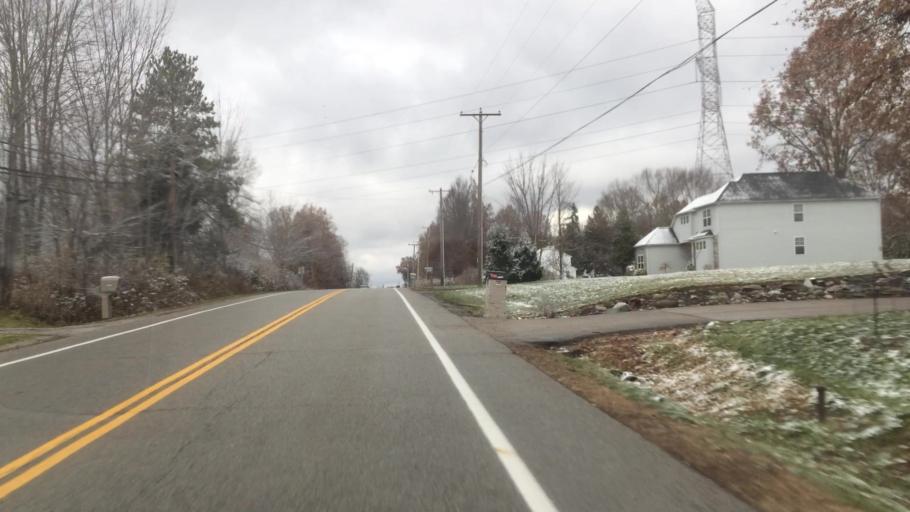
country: US
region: Ohio
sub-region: Summit County
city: Macedonia
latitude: 41.3054
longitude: -81.5319
